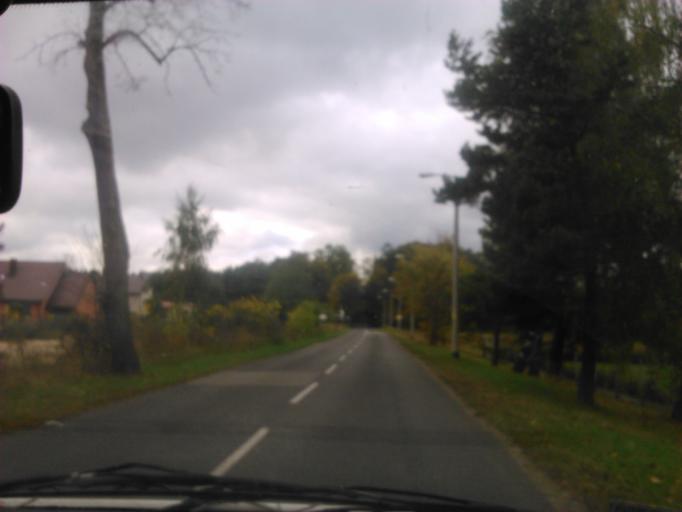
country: PL
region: Pomeranian Voivodeship
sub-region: Powiat gdanski
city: Cedry Wielkie
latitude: 54.3396
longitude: 18.8927
